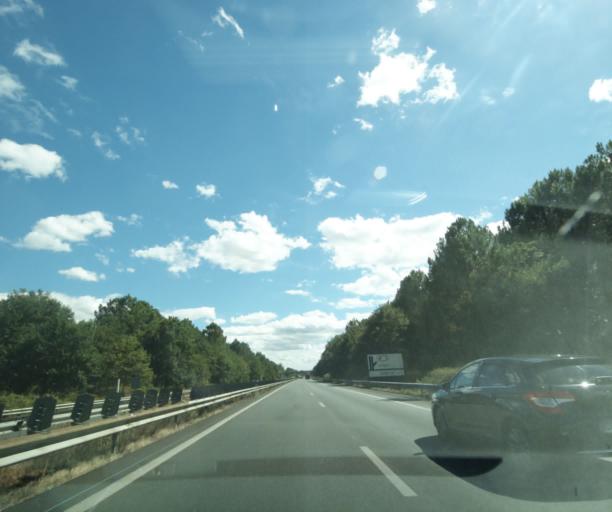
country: FR
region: Aquitaine
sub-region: Departement de la Gironde
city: Toulenne
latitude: 44.5563
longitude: -0.2848
